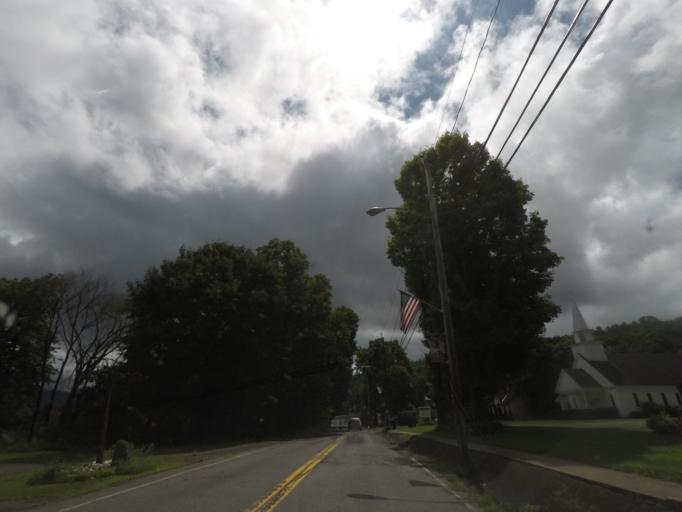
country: US
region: Massachusetts
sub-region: Berkshire County
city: Williamstown
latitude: 42.6948
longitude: -73.3742
